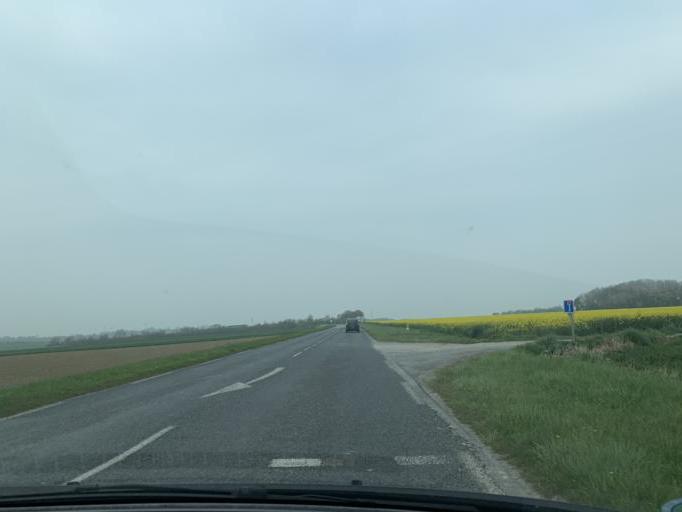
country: FR
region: Nord-Pas-de-Calais
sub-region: Departement du Pas-de-Calais
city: Montreuil
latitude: 50.4242
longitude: 1.7281
